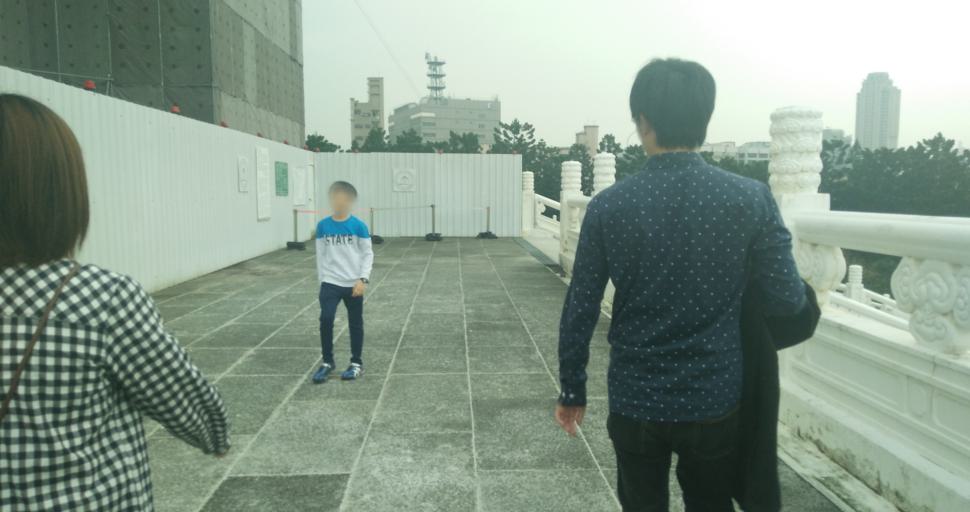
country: TW
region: Taipei
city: Taipei
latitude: 25.0345
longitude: 121.5215
